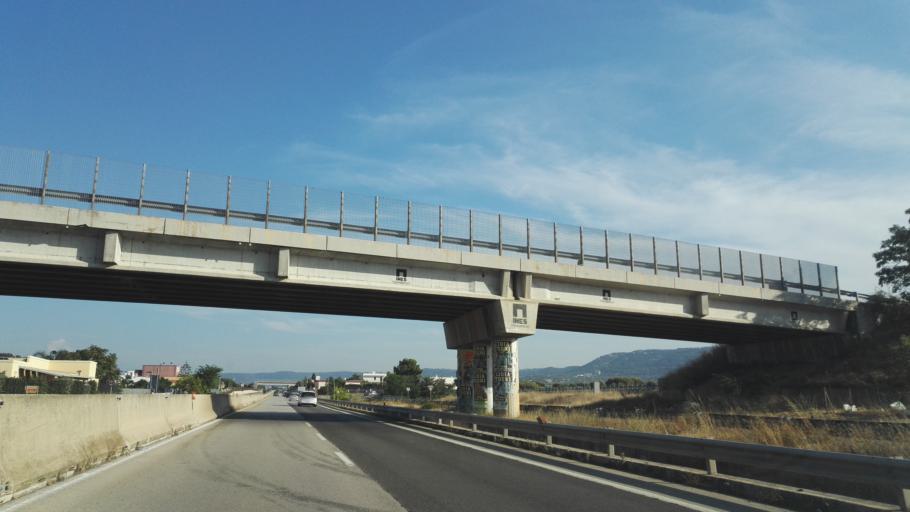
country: IT
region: Apulia
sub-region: Provincia di Brindisi
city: Fasano
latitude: 40.8731
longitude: 17.3421
